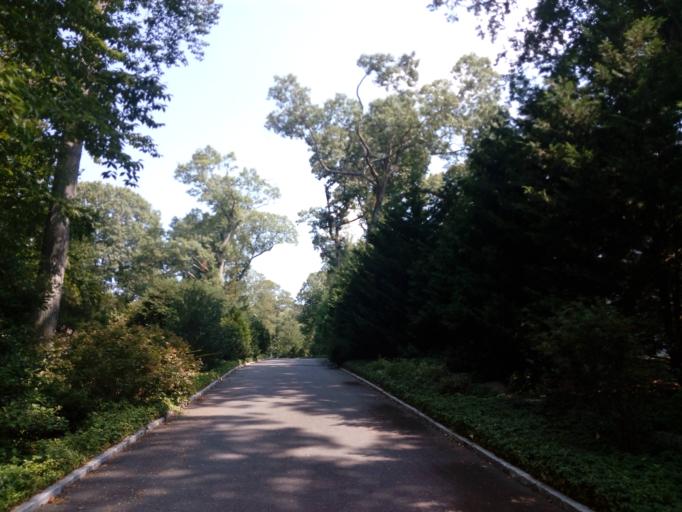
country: US
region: New York
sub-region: Nassau County
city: Locust Valley
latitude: 40.8595
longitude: -73.5942
